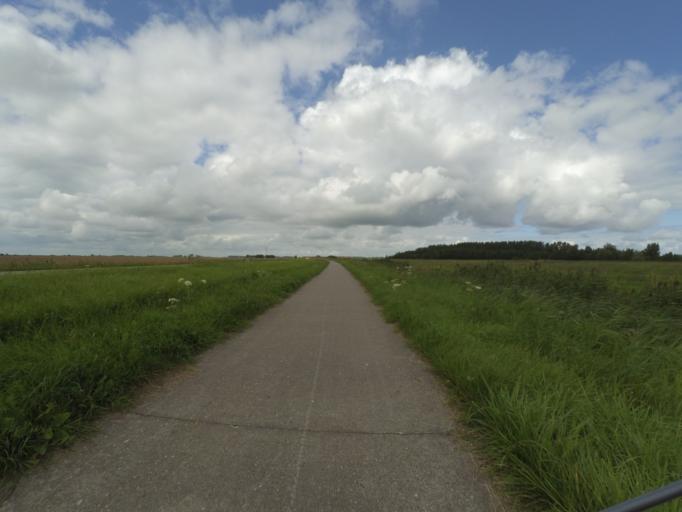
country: NL
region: Groningen
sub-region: Gemeente Zuidhorn
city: Grijpskerk
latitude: 53.3204
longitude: 6.2454
